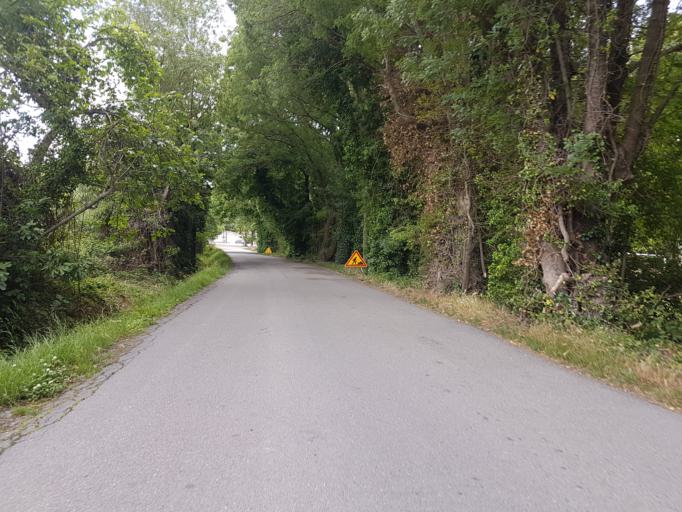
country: FR
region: Languedoc-Roussillon
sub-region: Departement du Gard
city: Beaucaire
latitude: 43.8146
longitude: 4.6423
